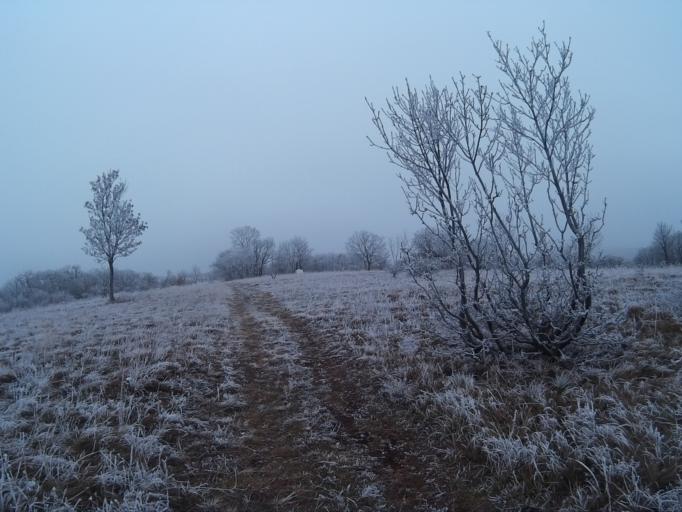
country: HU
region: Fejer
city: Csakvar
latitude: 47.3898
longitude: 18.3989
